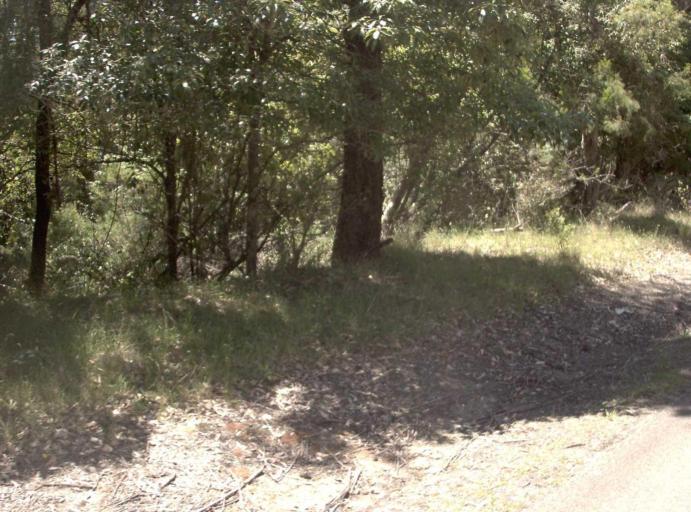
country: AU
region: Victoria
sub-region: East Gippsland
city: Lakes Entrance
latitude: -37.7064
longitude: 148.5748
